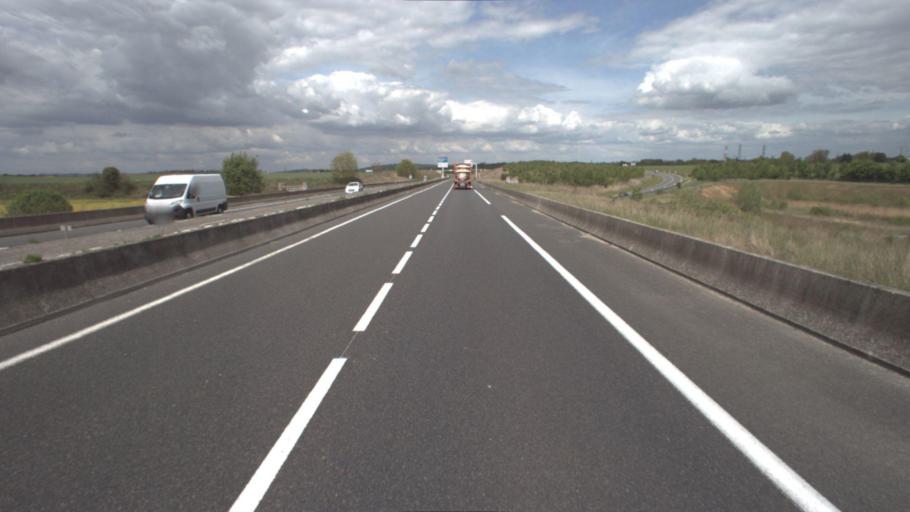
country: FR
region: Ile-de-France
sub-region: Departement de Seine-et-Marne
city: Villenoy
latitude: 48.9342
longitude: 2.8463
